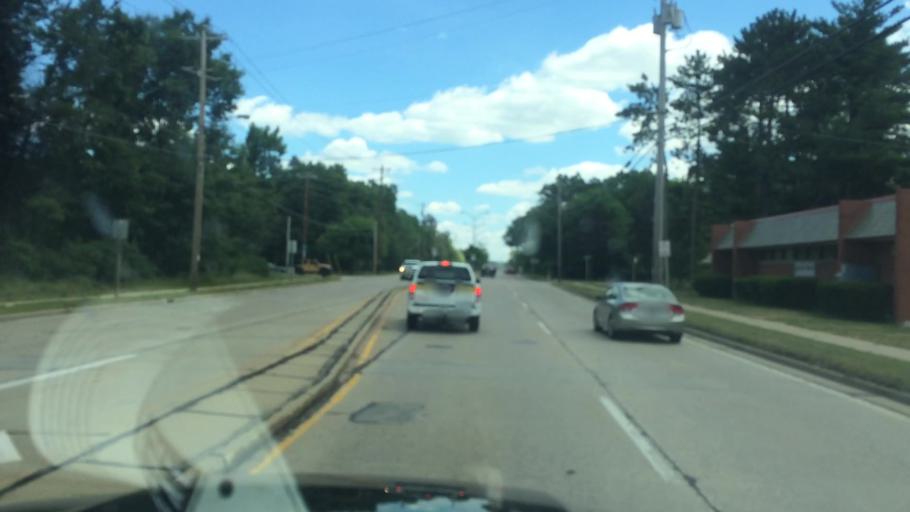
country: US
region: Wisconsin
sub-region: Portage County
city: Stevens Point
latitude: 44.5233
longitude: -89.5456
